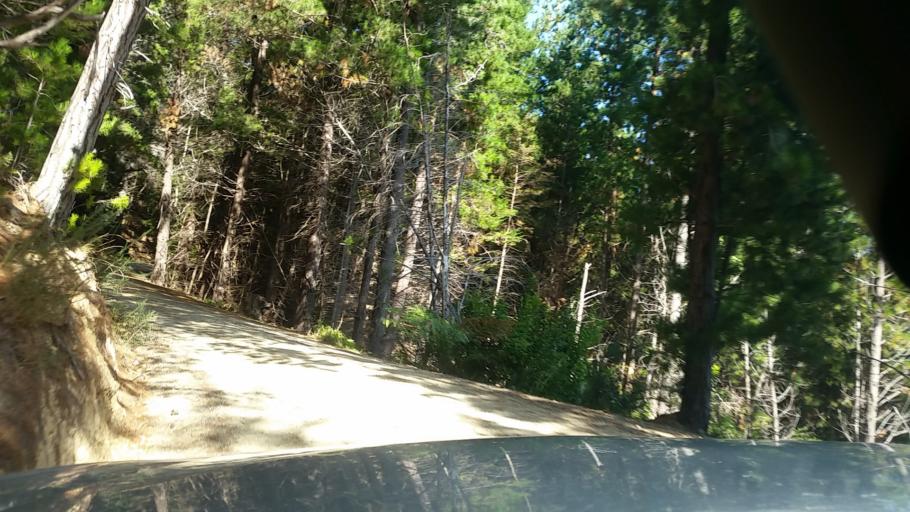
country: NZ
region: Marlborough
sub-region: Marlborough District
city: Picton
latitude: -41.2981
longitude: 174.1821
